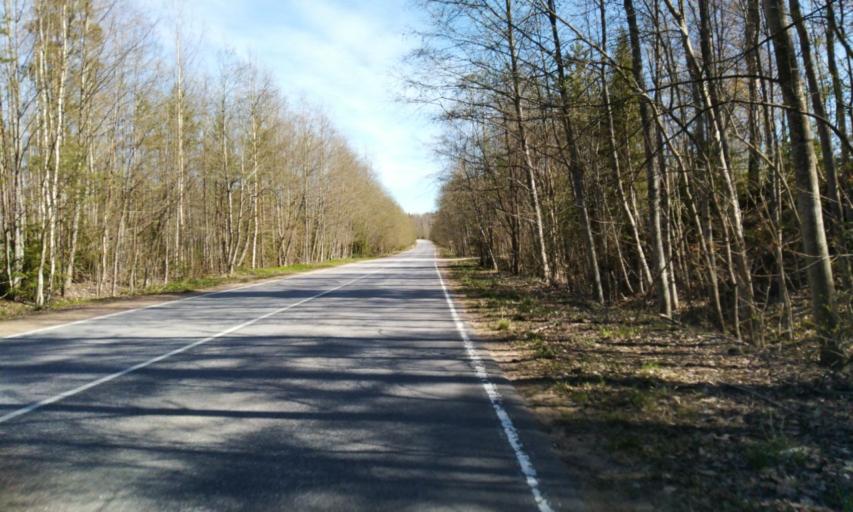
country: RU
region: Leningrad
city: Garbolovo
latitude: 60.4193
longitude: 30.4609
